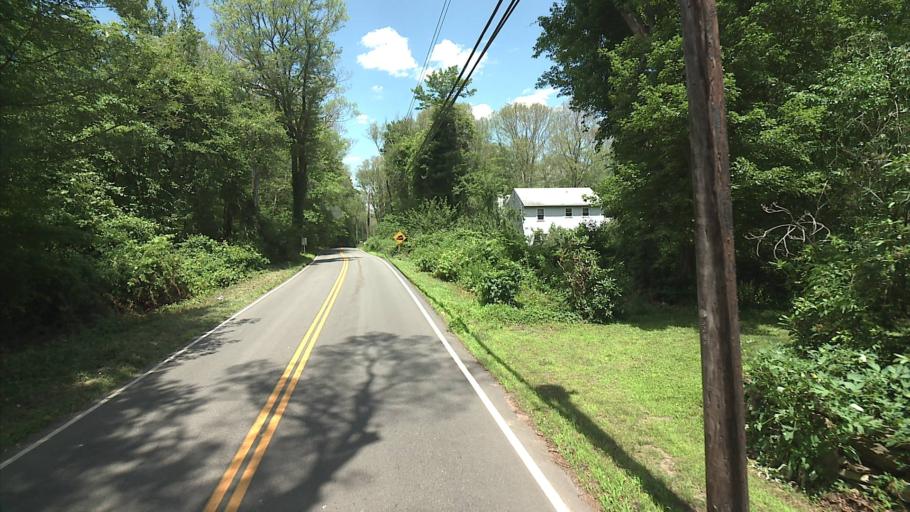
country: US
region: Connecticut
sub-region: New London County
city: Colchester
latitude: 41.4888
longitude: -72.3537
